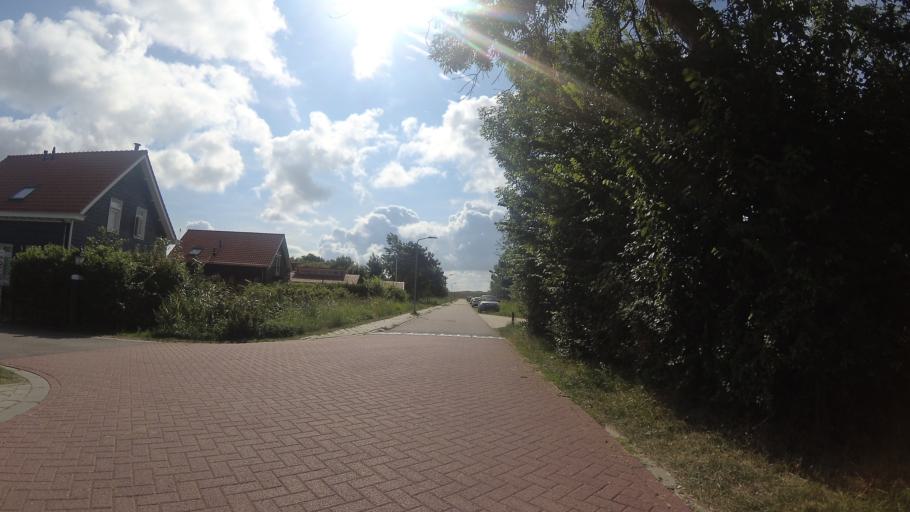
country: NL
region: Zeeland
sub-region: Schouwen-Duiveland
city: Burgh
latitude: 51.6728
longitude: 3.7107
